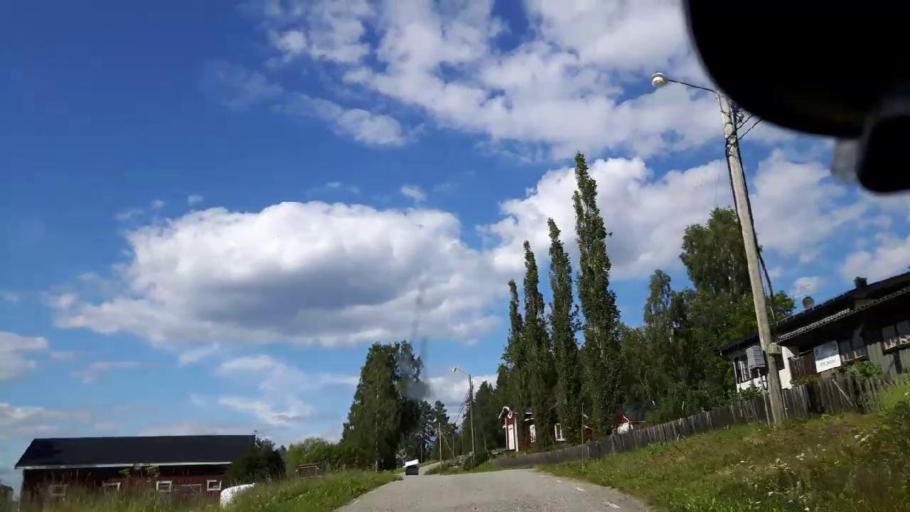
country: SE
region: Jaemtland
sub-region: Braecke Kommun
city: Braecke
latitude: 62.8697
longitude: 15.2721
